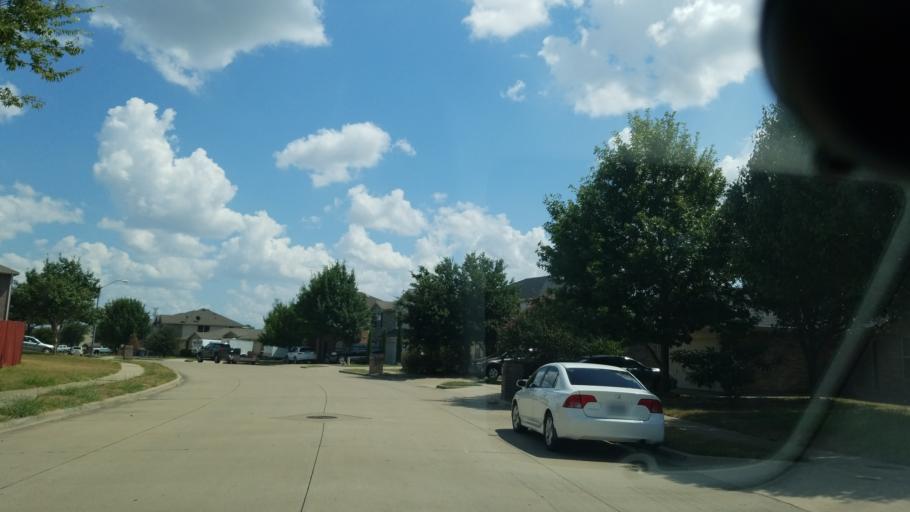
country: US
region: Texas
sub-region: Dallas County
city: Grand Prairie
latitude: 32.7328
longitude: -96.9914
